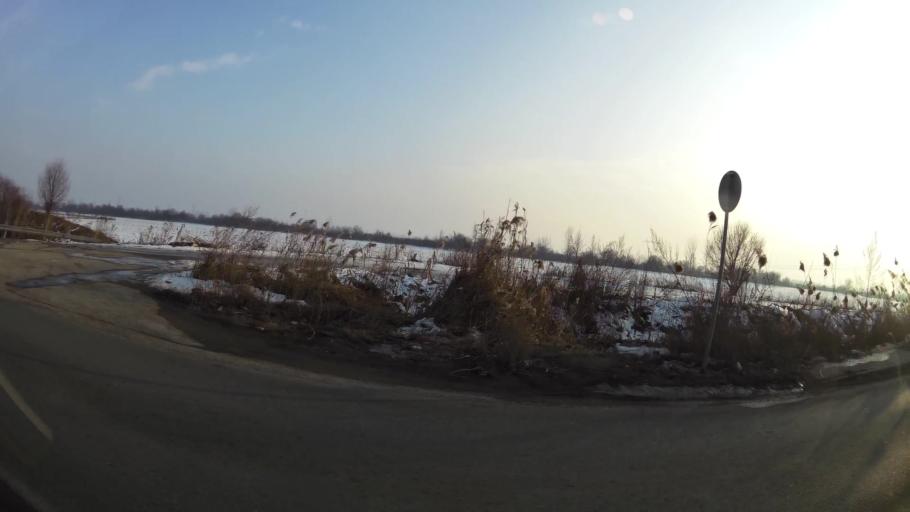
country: MK
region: Aracinovo
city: Arachinovo
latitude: 42.0192
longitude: 21.5368
